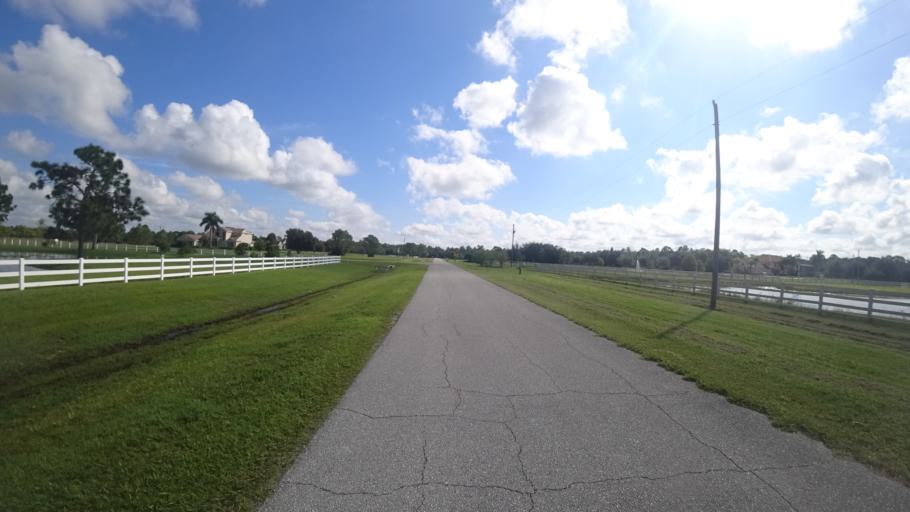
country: US
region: Florida
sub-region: Sarasota County
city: The Meadows
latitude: 27.3984
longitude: -82.3334
